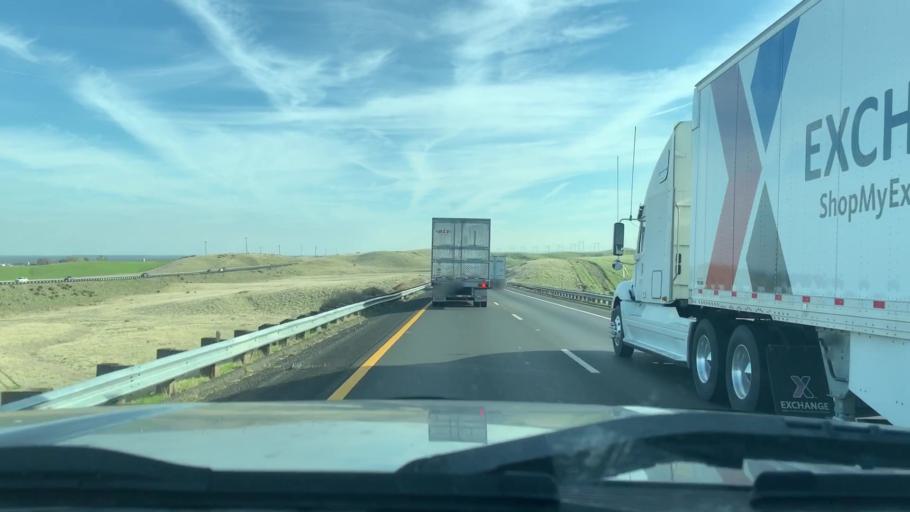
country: US
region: California
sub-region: Fresno County
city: Coalinga
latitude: 36.3172
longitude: -120.2891
